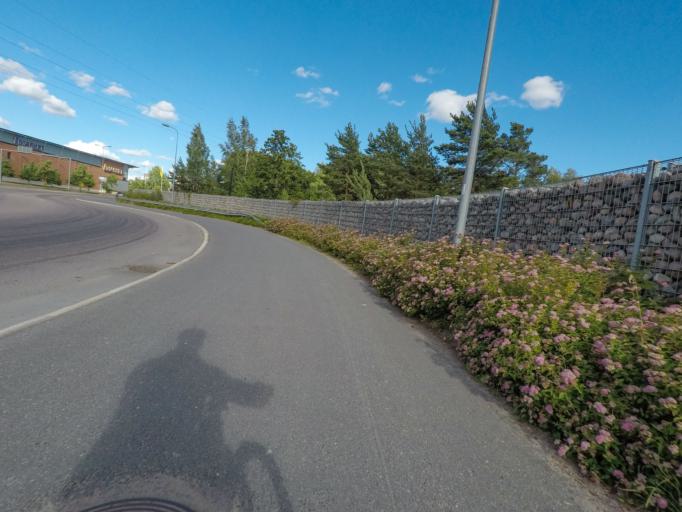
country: FI
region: South Karelia
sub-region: Lappeenranta
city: Lappeenranta
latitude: 61.0639
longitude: 28.1698
